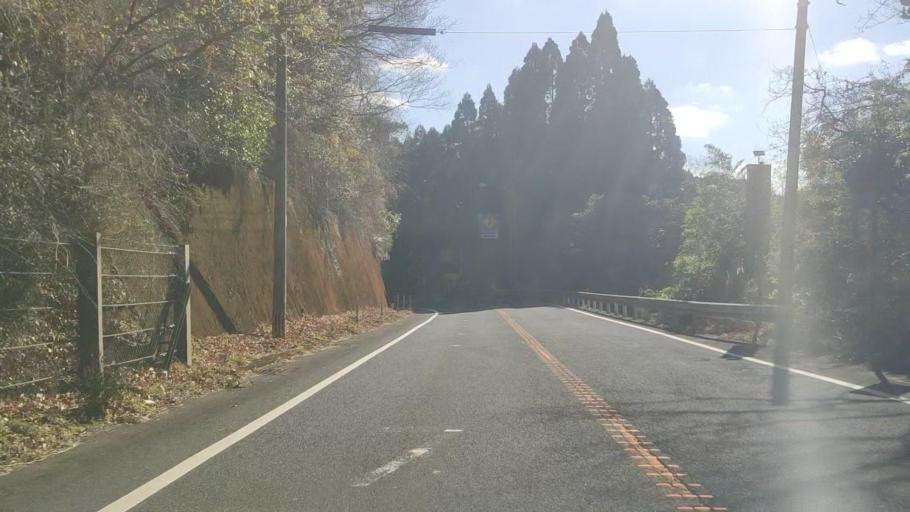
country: JP
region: Kagoshima
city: Sueyoshicho-ninokata
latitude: 31.6632
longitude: 130.8843
